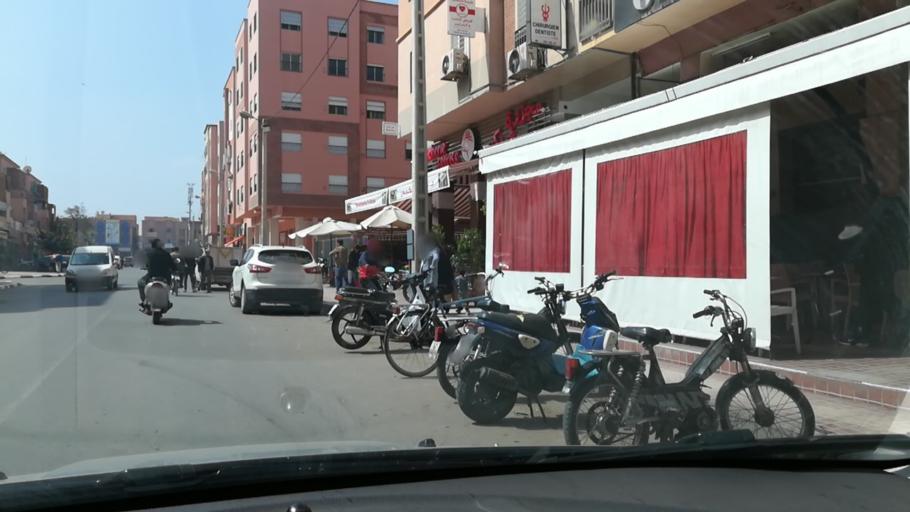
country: MA
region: Marrakech-Tensift-Al Haouz
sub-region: Marrakech
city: Marrakesh
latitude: 31.6298
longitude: -8.0625
